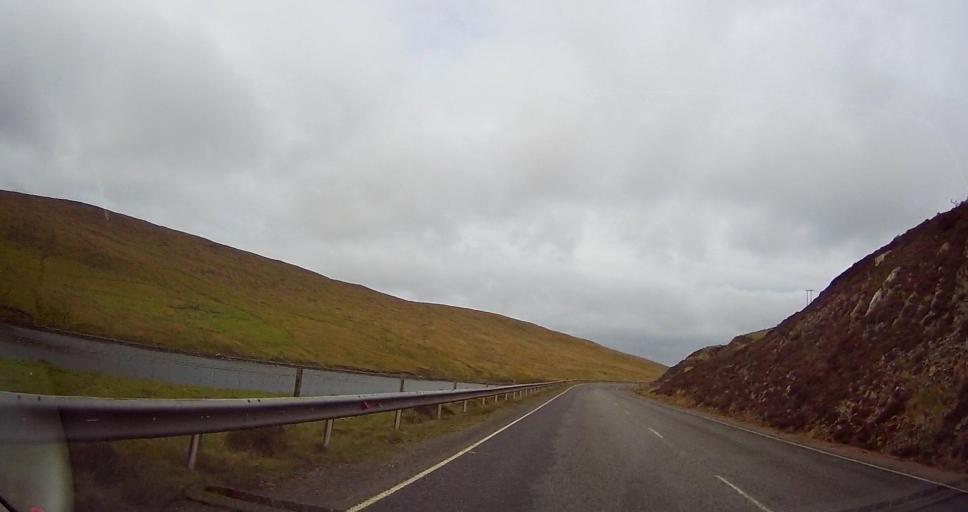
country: GB
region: Scotland
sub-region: Shetland Islands
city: Lerwick
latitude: 60.3563
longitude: -1.2791
